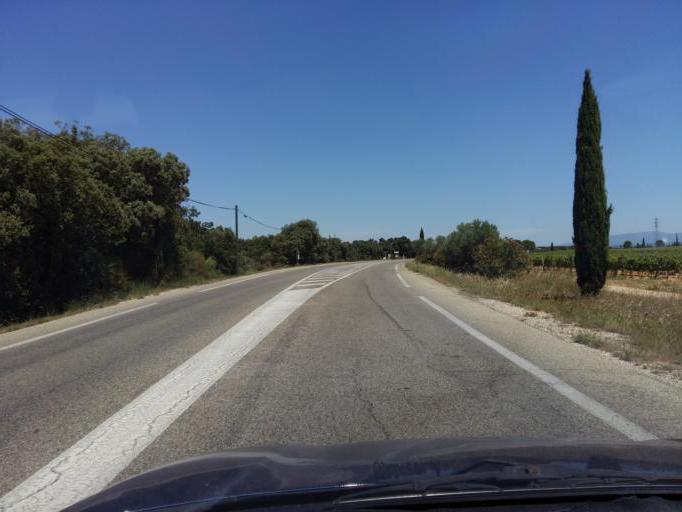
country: FR
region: Provence-Alpes-Cote d'Azur
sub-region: Departement du Vaucluse
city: Serignan-du-Comtat
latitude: 44.2117
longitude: 4.8685
